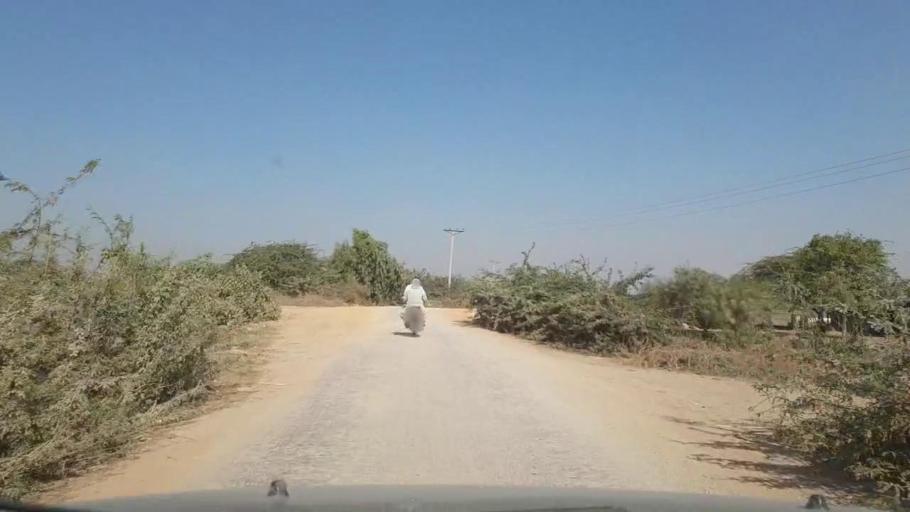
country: PK
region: Sindh
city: Thatta
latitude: 24.7952
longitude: 67.9018
